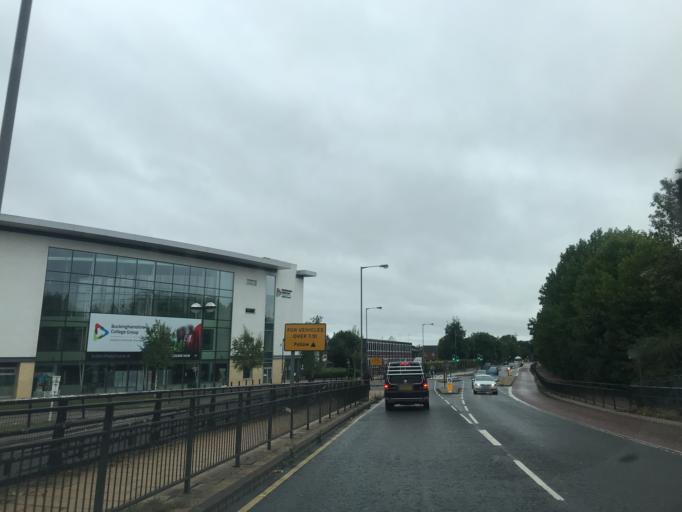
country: GB
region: England
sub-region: Buckinghamshire
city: Aylesbury
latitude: 51.8149
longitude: -0.8231
